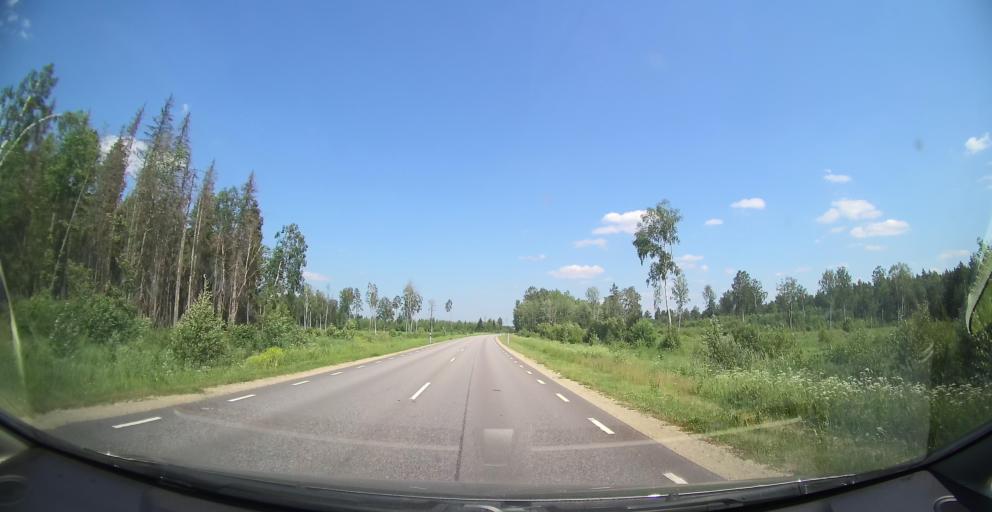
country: EE
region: Harju
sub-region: Anija vald
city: Kehra
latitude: 59.2443
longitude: 25.2989
